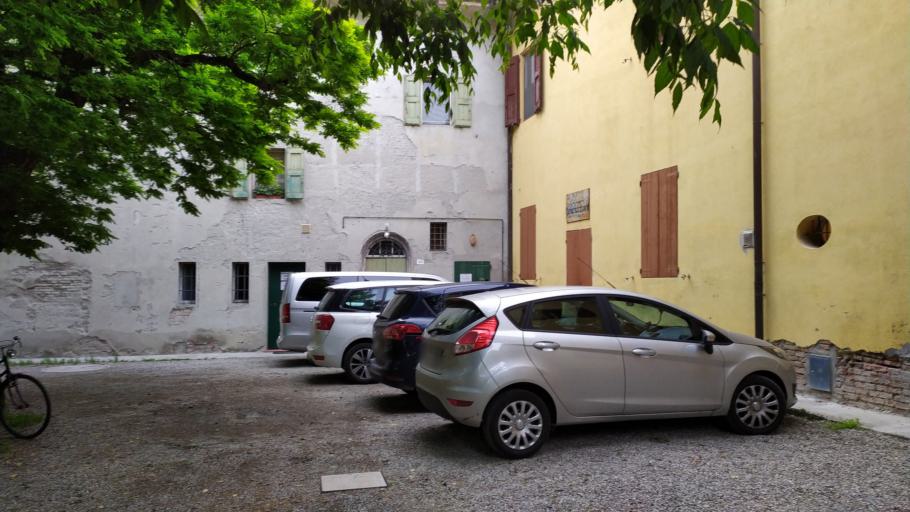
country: IT
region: Emilia-Romagna
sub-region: Provincia di Bologna
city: Castel Maggiore
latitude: 44.5824
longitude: 11.3582
